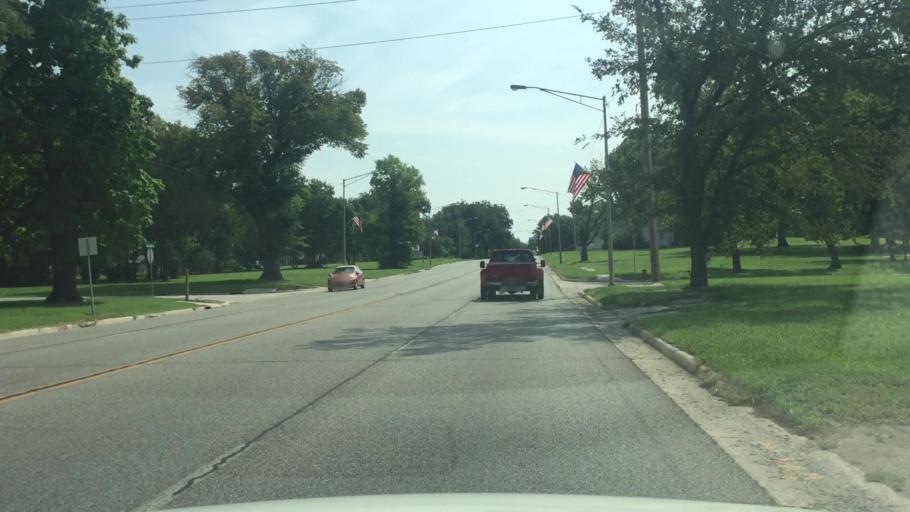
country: US
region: Kansas
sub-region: Montgomery County
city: Coffeyville
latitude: 37.0328
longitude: -95.6129
